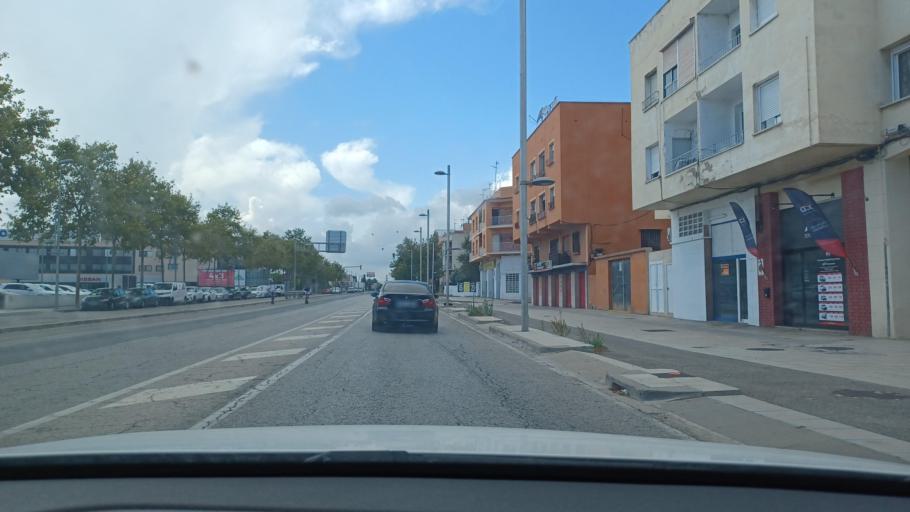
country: ES
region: Catalonia
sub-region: Provincia de Tarragona
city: Tarragona
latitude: 41.1155
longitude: 1.2204
